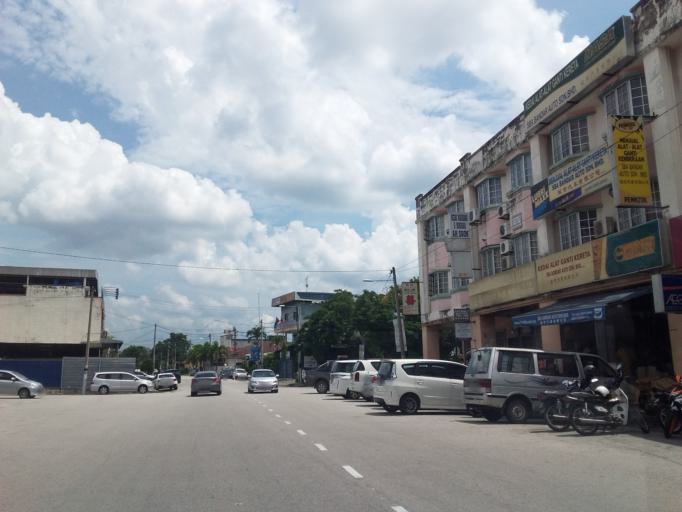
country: MY
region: Johor
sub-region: Daerah Batu Pahat
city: Batu Pahat
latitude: 1.8551
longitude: 102.9293
